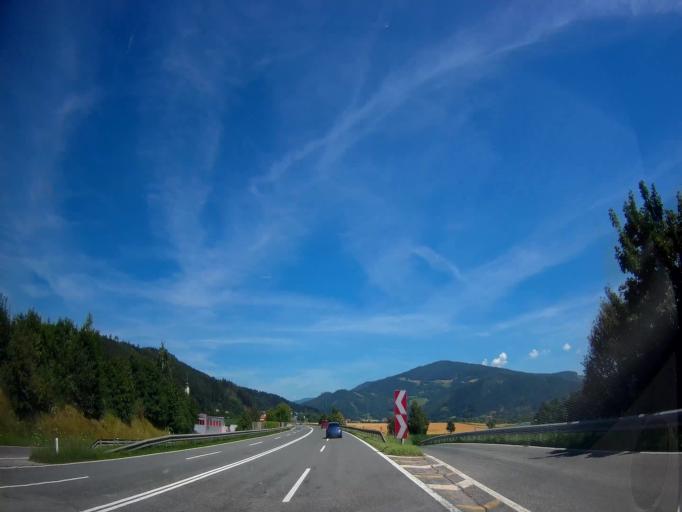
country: AT
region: Carinthia
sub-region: Politischer Bezirk Sankt Veit an der Glan
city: Molbling
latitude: 46.8615
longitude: 14.4498
